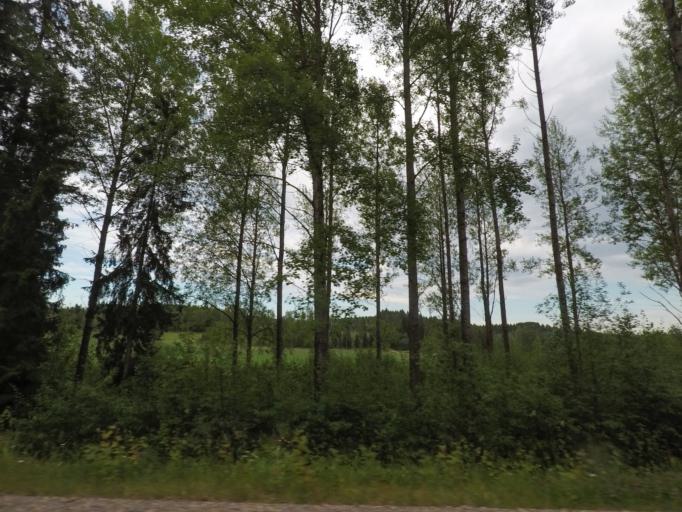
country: FI
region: Uusimaa
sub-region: Porvoo
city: Pukkila
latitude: 60.7652
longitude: 25.4460
